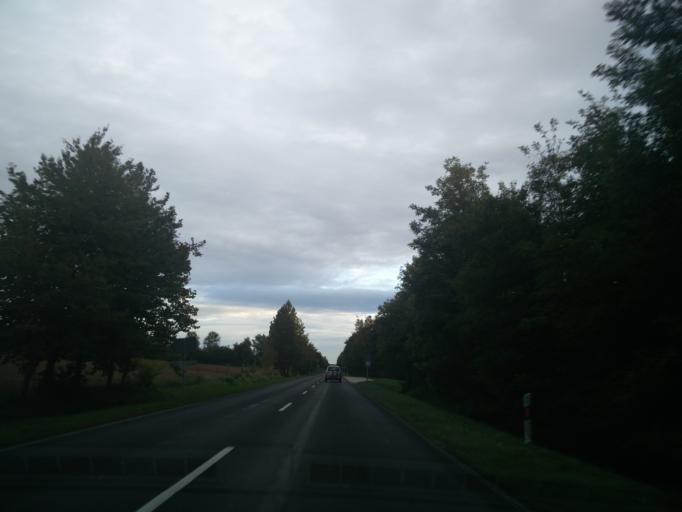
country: HU
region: Zala
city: Keszthely
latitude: 46.7505
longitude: 17.2182
